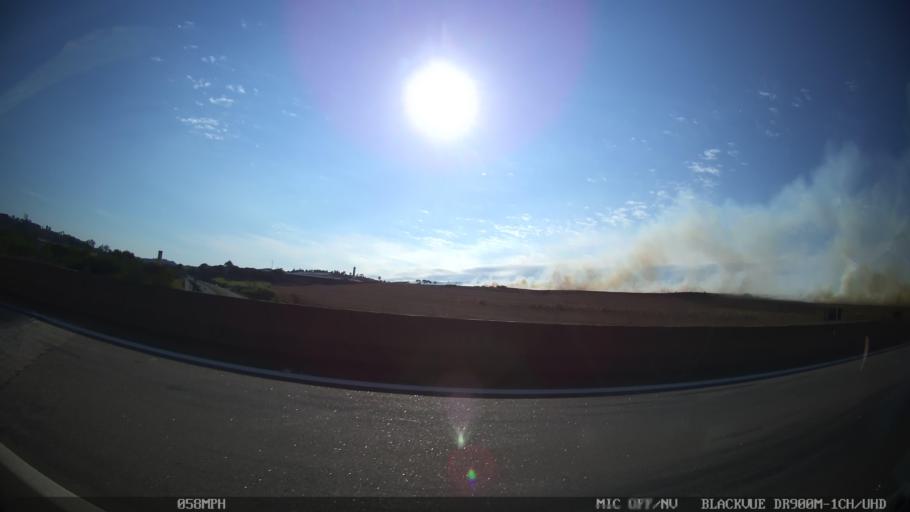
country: BR
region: Sao Paulo
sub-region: Piracicaba
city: Piracicaba
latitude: -22.6996
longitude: -47.6077
